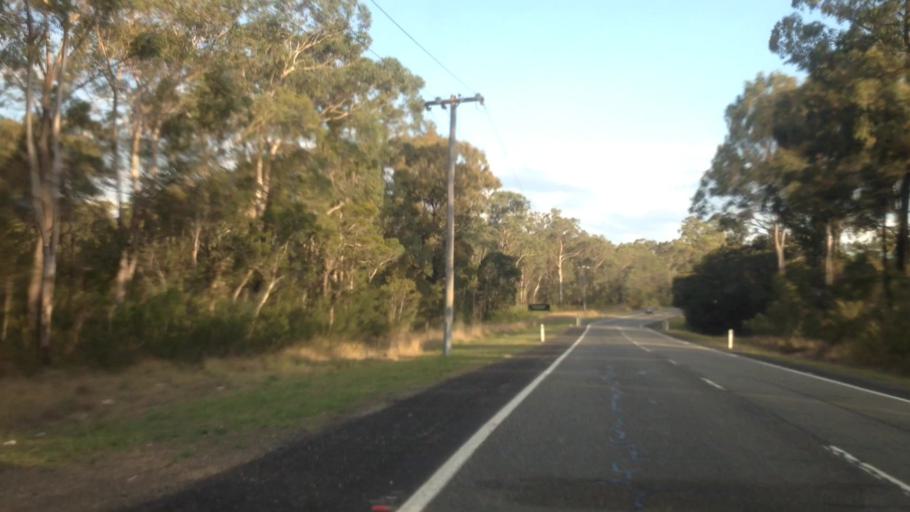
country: AU
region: New South Wales
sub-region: Cessnock
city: Kurri Kurri
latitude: -32.8375
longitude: 151.4827
